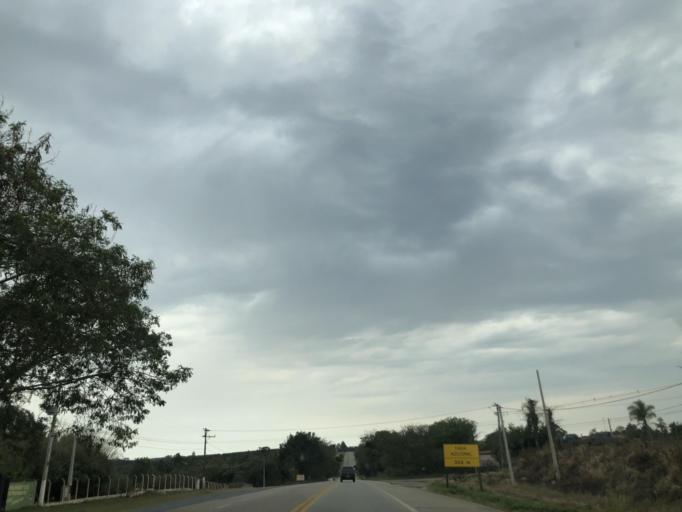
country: BR
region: Sao Paulo
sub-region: Salto De Pirapora
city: Salto de Pirapora
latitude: -23.7085
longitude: -47.6342
